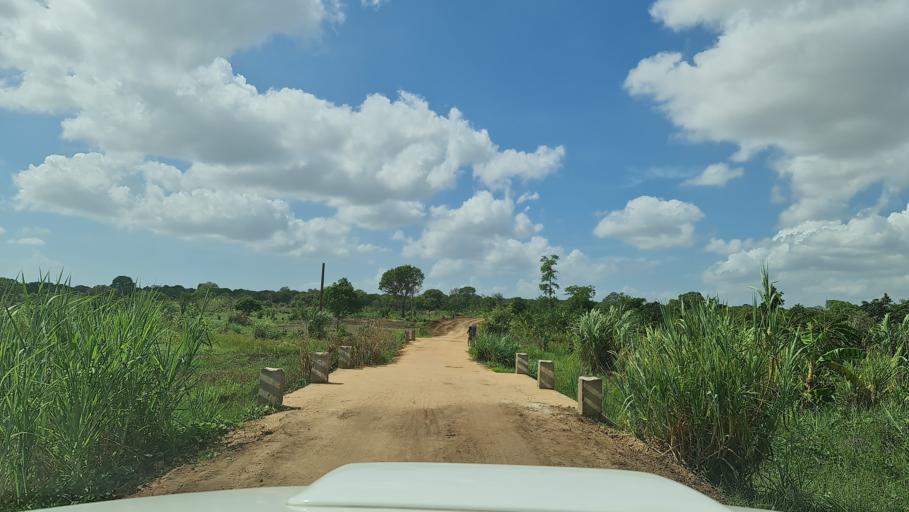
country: MZ
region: Nampula
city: Ilha de Mocambique
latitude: -15.0121
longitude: 40.5603
